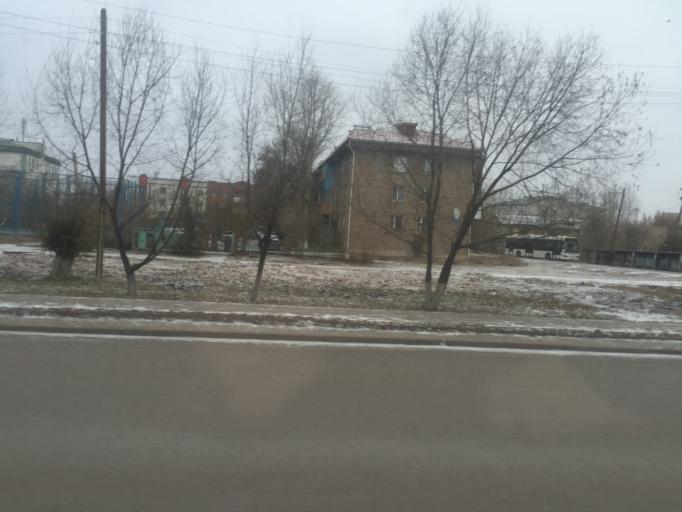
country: KZ
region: Astana Qalasy
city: Astana
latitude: 51.1992
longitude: 71.3910
